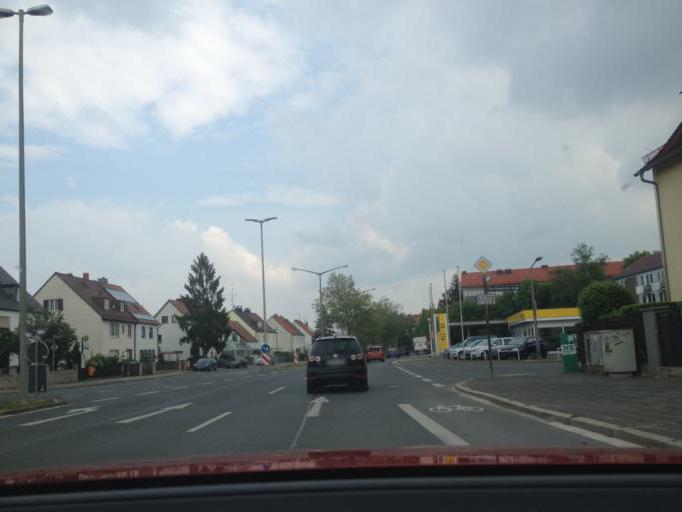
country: DE
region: Bavaria
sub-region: Regierungsbezirk Mittelfranken
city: Grossreuth bei Schweinau
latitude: 49.4415
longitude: 11.0308
